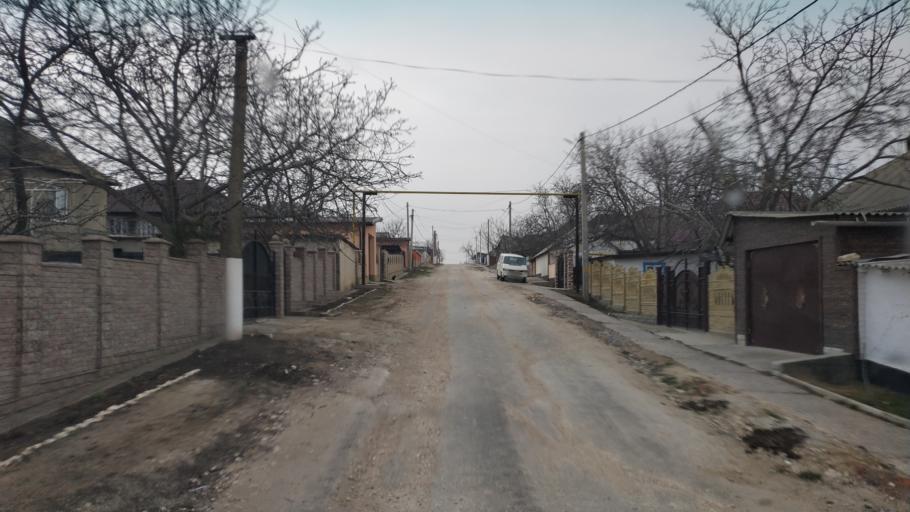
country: MD
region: Chisinau
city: Singera
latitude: 46.8234
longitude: 28.9654
